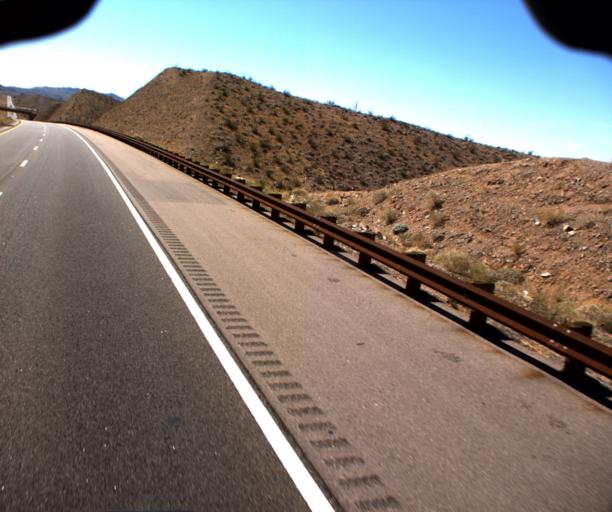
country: US
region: Nevada
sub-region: Clark County
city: Boulder City
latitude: 35.8930
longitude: -114.6246
